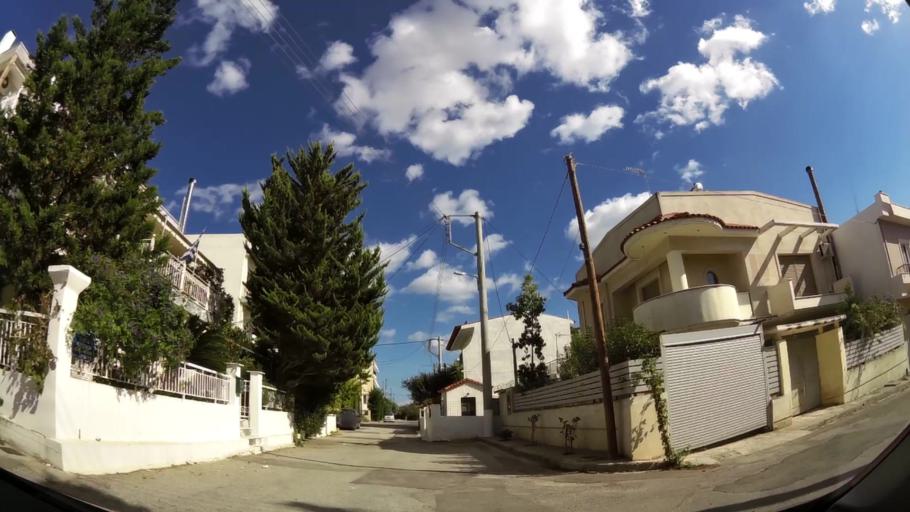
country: GR
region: Attica
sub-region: Nomarchia Anatolikis Attikis
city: Acharnes
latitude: 38.0991
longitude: 23.7311
